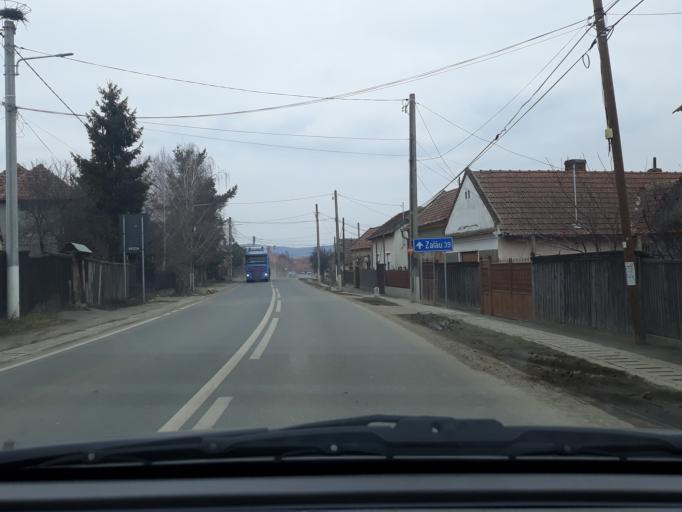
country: RO
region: Salaj
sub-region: Comuna Nusfalau
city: Nusfalau
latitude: 47.1910
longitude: 22.7015
